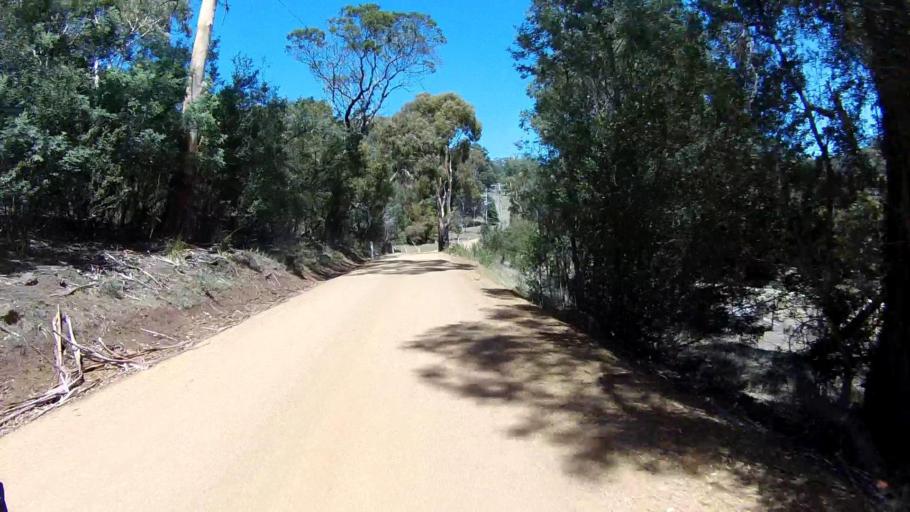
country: AU
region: Tasmania
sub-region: Clarence
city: Cambridge
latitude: -42.8507
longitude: 147.4382
